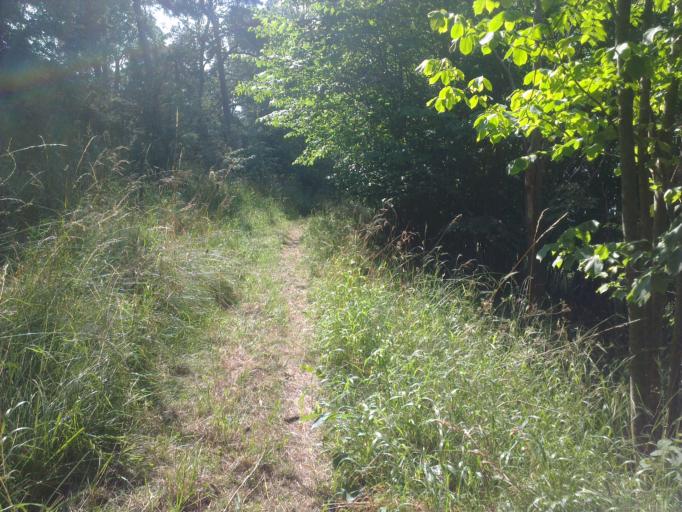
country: DK
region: Capital Region
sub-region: Frederikssund Kommune
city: Skibby
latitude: 55.7757
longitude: 12.0308
